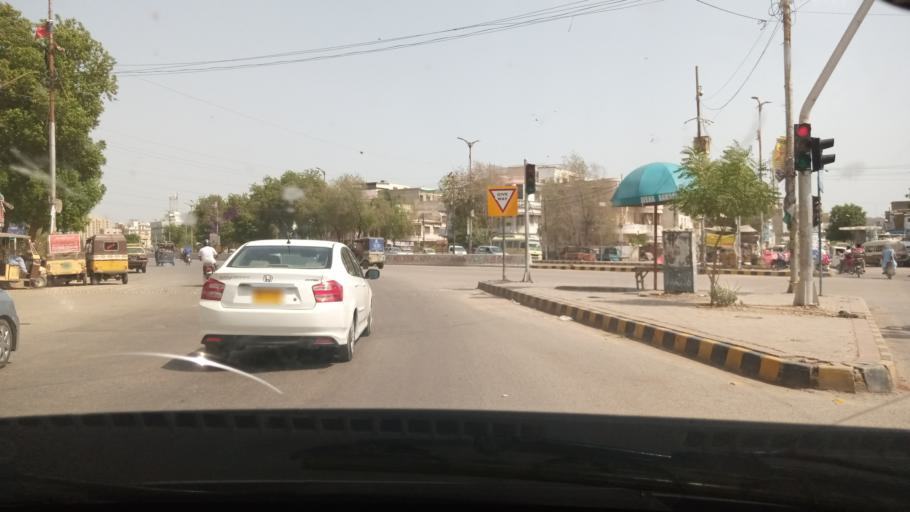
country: PK
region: Sindh
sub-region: Karachi District
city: Karachi
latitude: 24.8708
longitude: 67.0478
